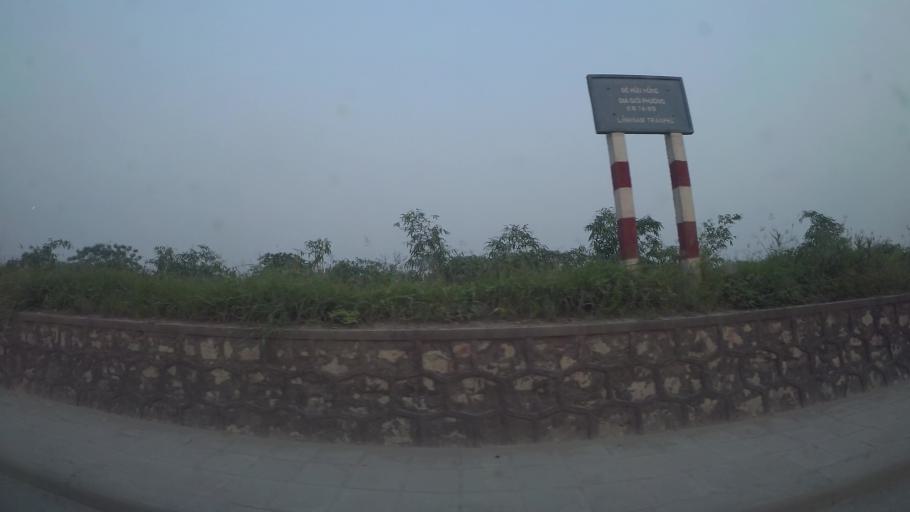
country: VN
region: Hung Yen
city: Van Giang
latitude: 20.9761
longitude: 105.8896
